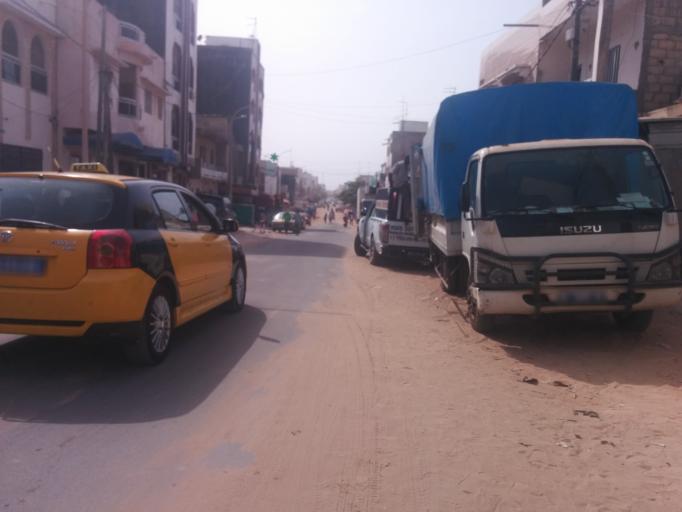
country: SN
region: Dakar
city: Pikine
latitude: 14.7645
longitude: -17.4383
